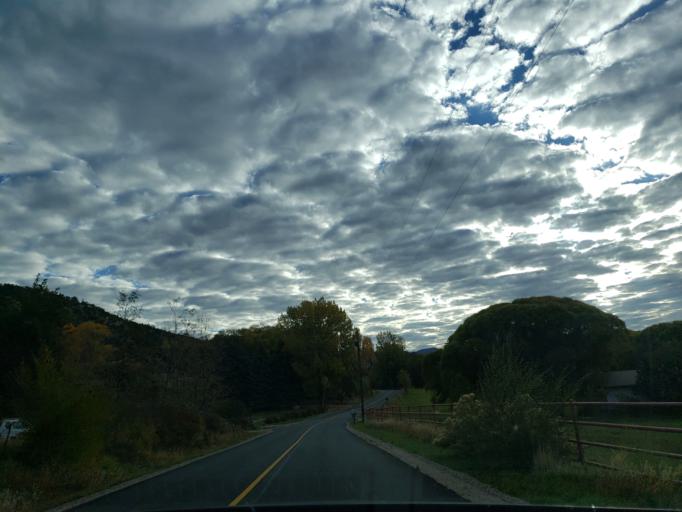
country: US
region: Colorado
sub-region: Garfield County
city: New Castle
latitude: 39.5605
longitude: -107.5656
